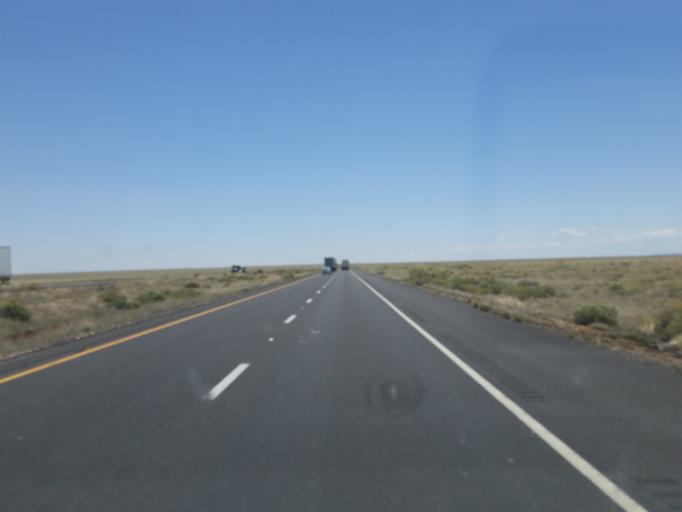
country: US
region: Arizona
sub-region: Coconino County
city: Flagstaff
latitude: 35.1453
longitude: -111.2284
